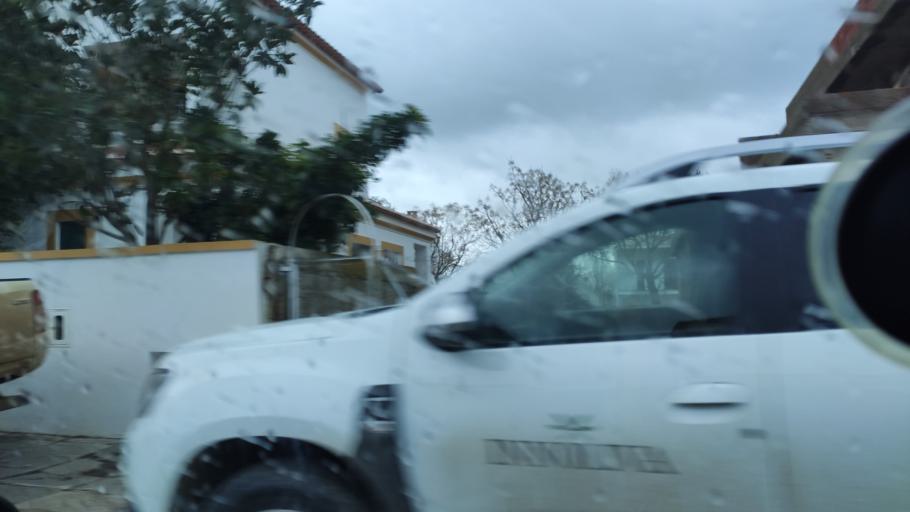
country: PT
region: Beja
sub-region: Beja
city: Beja
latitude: 38.0177
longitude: -7.8530
